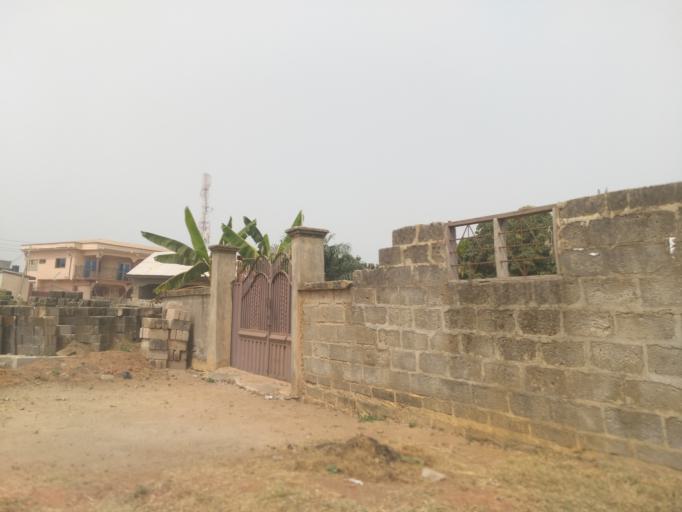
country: GH
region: Ashanti
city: Mamponteng
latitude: 6.6653
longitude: -1.5468
